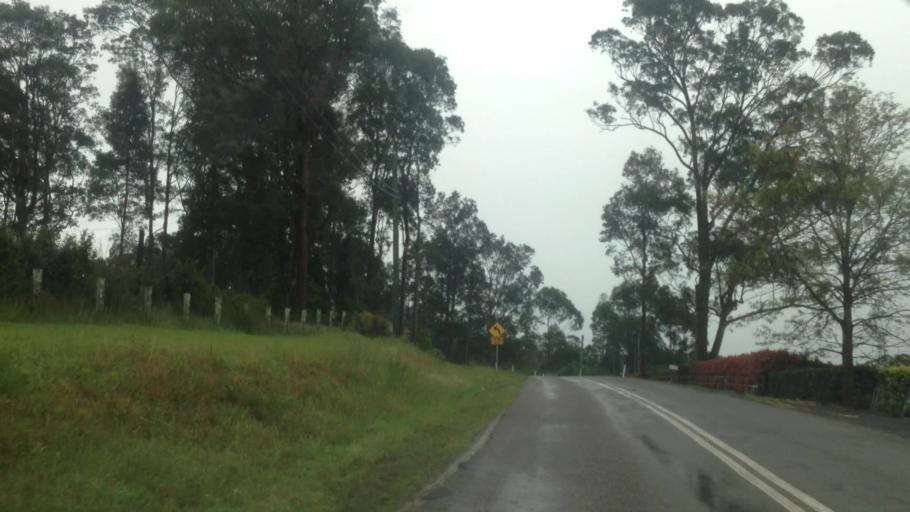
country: AU
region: New South Wales
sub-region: Wyong Shire
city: Little Jilliby
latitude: -33.2410
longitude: 151.3815
